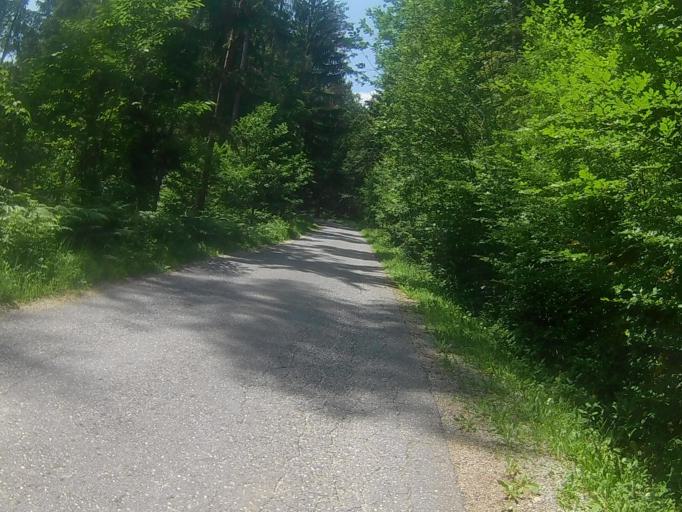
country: SI
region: Ruse
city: Bistrica ob Dravi
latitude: 46.5837
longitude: 15.5479
